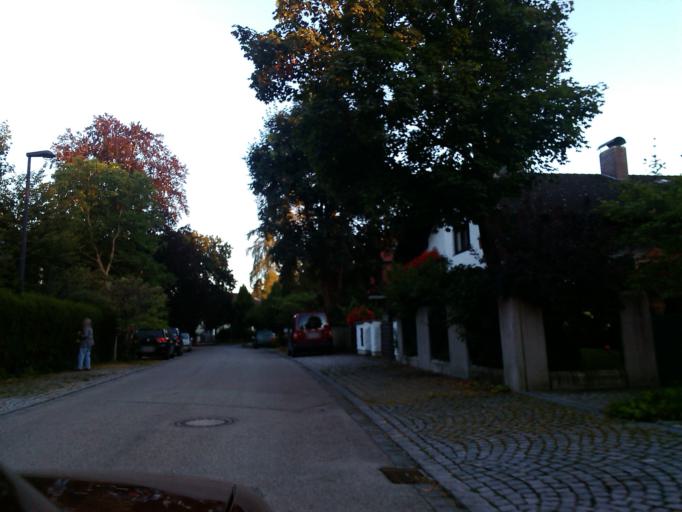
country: DE
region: Bavaria
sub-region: Upper Bavaria
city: Planegg
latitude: 48.1085
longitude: 11.4202
